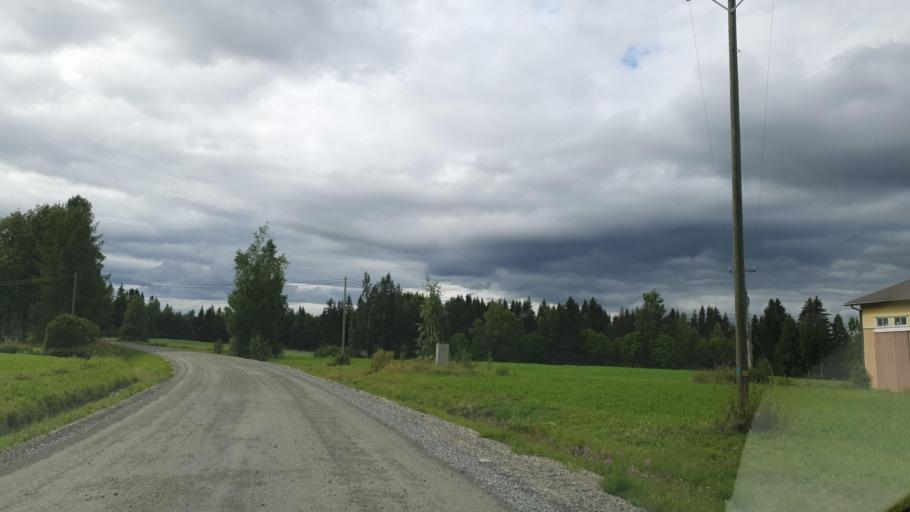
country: FI
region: Northern Savo
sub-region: Ylae-Savo
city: Iisalmi
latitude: 63.5364
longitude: 27.0826
